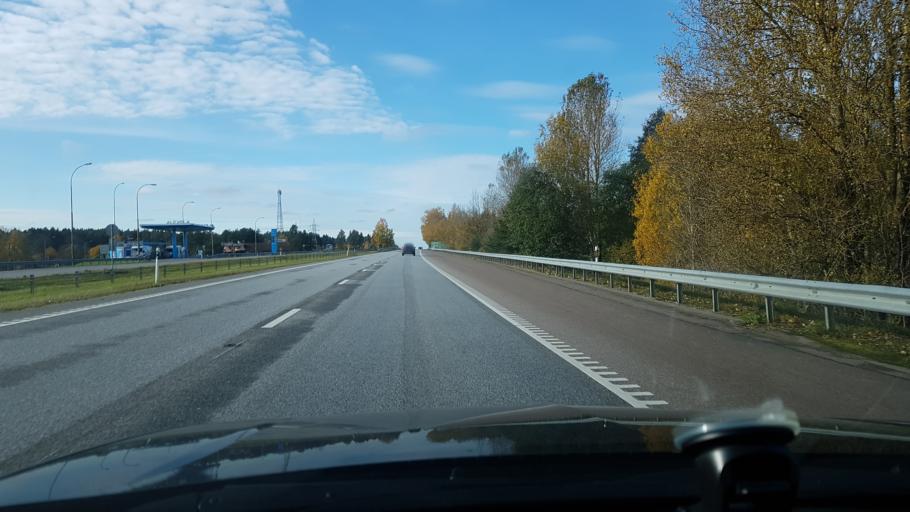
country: EE
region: Harju
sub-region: Kuusalu vald
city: Kuusalu
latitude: 59.4489
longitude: 25.4379
